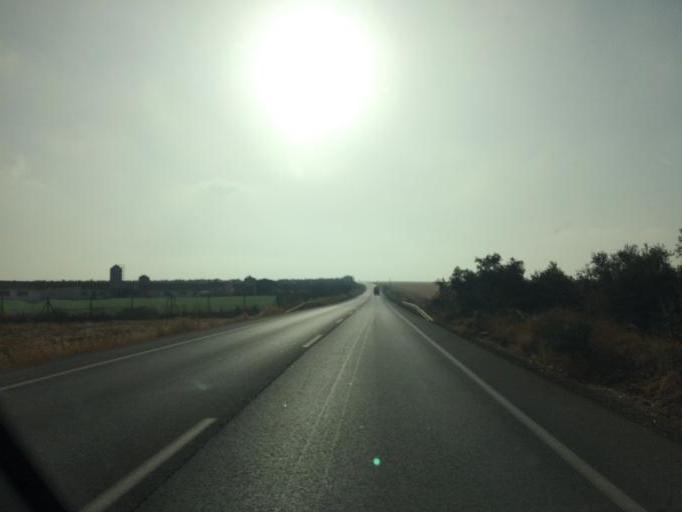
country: ES
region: Andalusia
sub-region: Provincia de Malaga
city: Campillos
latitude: 37.0493
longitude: -4.8245
